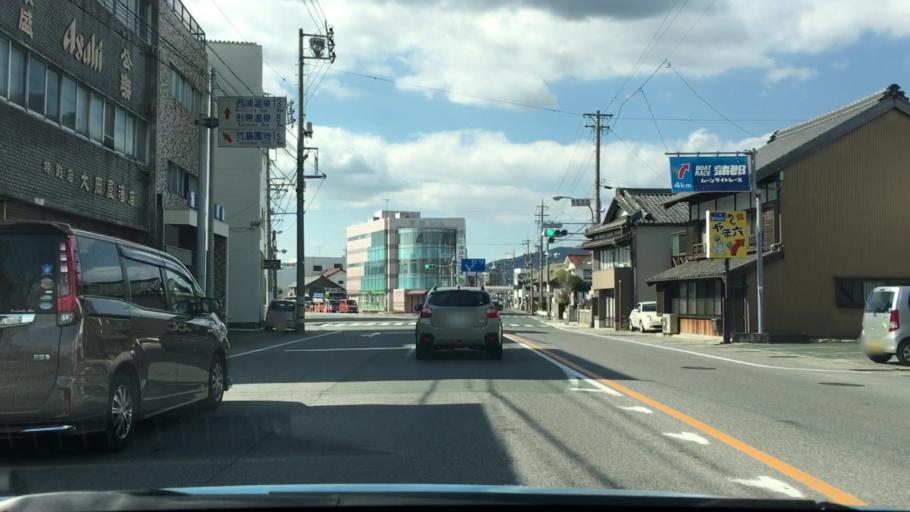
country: JP
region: Aichi
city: Gamagori
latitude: 34.8145
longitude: 137.2475
